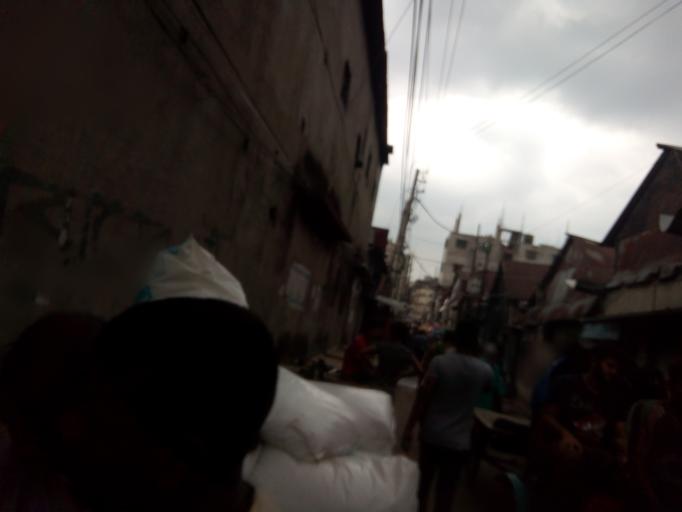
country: BD
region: Dhaka
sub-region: Dhaka
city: Dhaka
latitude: 23.7127
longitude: 90.3940
